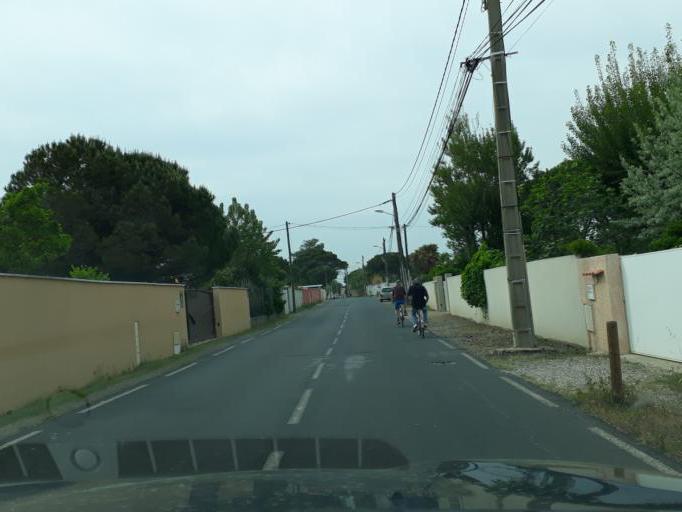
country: FR
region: Languedoc-Roussillon
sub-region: Departement de l'Herault
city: Agde
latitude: 43.2797
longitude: 3.4630
